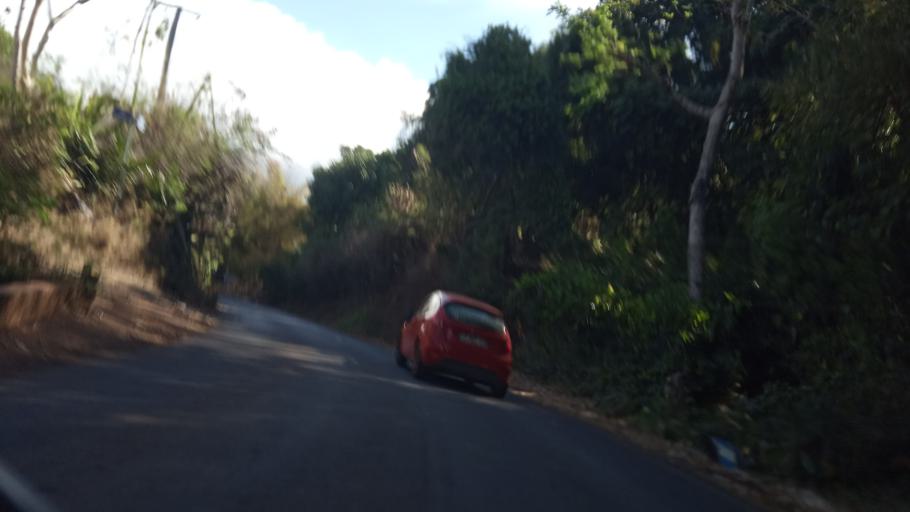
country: YT
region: Dembeni
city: Dembeni
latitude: -12.8213
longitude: 45.1941
